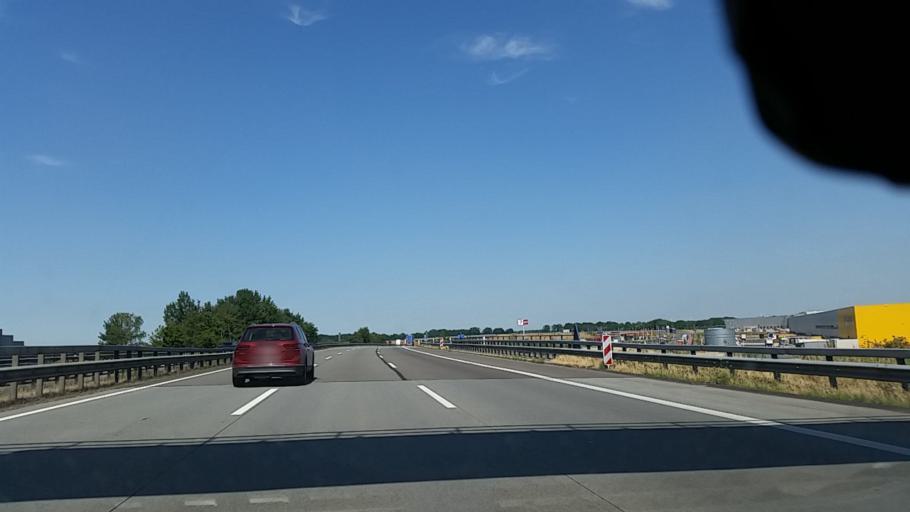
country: DE
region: Lower Saxony
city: Elsdorf
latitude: 53.2287
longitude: 9.3346
